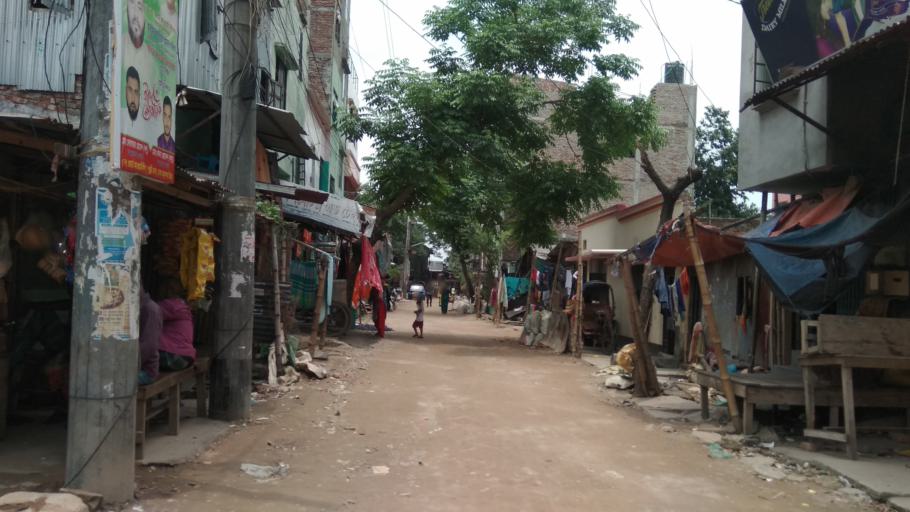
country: BD
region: Dhaka
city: Tungi
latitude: 23.8186
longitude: 90.3814
